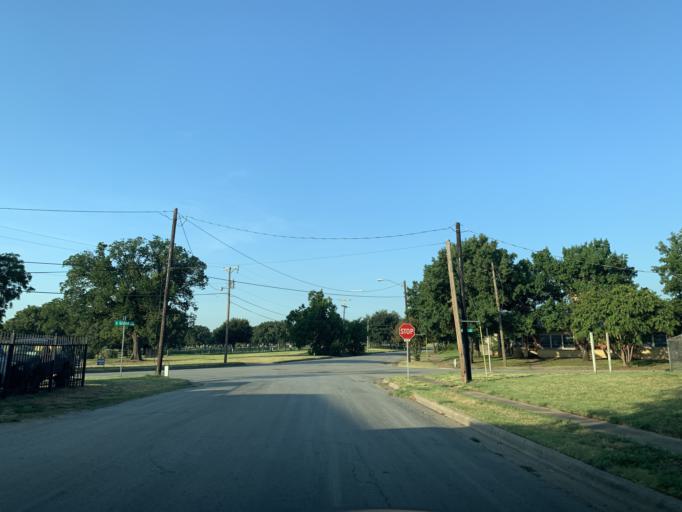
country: US
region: Texas
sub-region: Tarrant County
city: River Oaks
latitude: 32.7738
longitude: -97.3458
